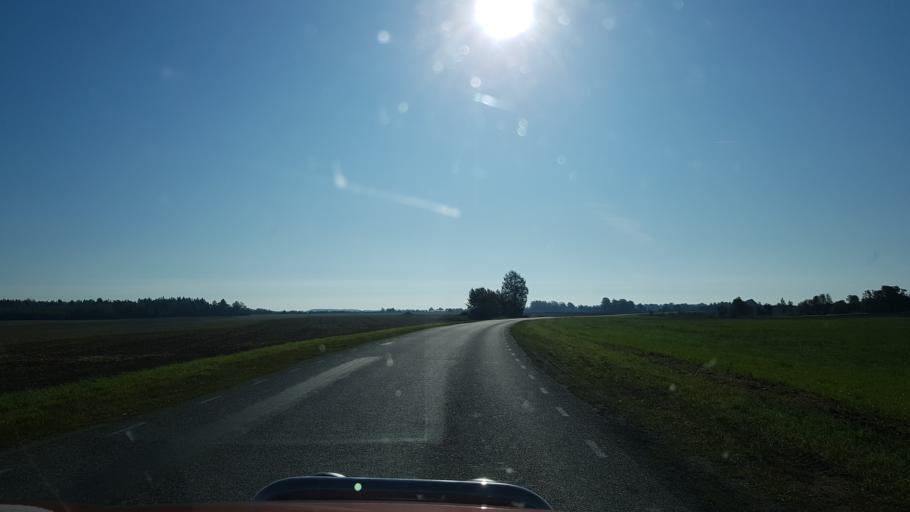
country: EE
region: Jogevamaa
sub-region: Tabivere vald
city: Tabivere
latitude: 58.6816
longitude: 26.6585
